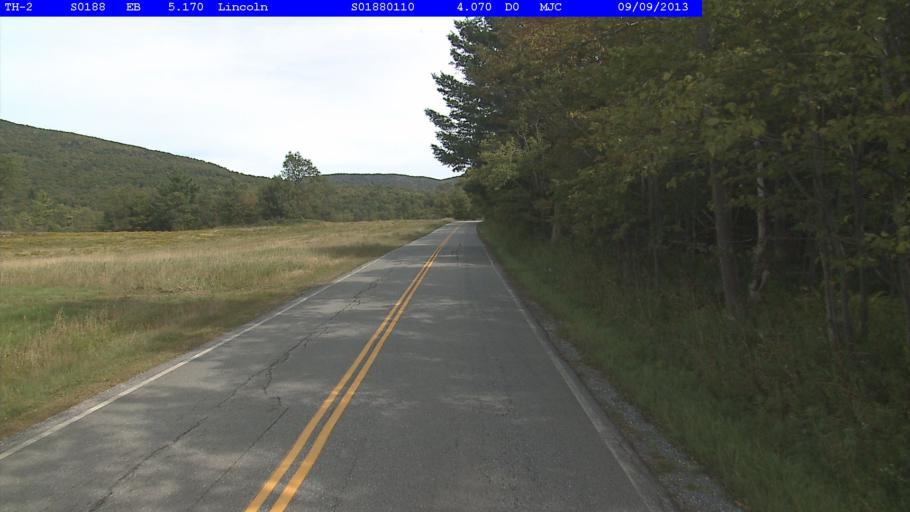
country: US
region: Vermont
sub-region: Addison County
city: Bristol
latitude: 44.0981
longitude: -72.9700
